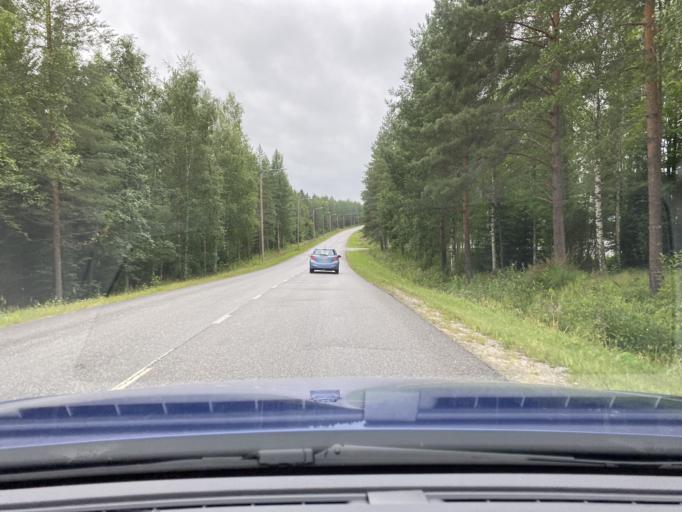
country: FI
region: Pirkanmaa
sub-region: Ylae-Pirkanmaa
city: Vilppula
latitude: 62.2441
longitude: 24.4739
